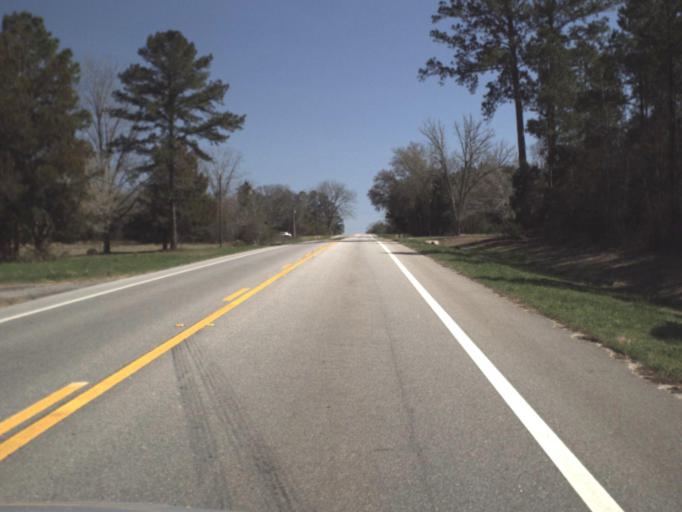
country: US
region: Florida
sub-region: Jackson County
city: Marianna
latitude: 30.8107
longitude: -85.2978
